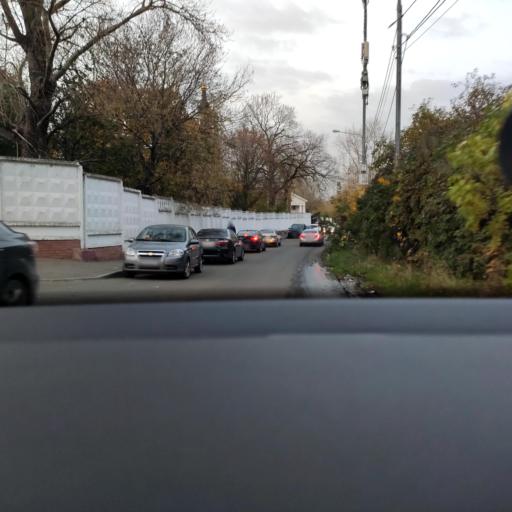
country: RU
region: Moscow
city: Orekhovo-Borisovo
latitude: 55.6287
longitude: 37.7282
